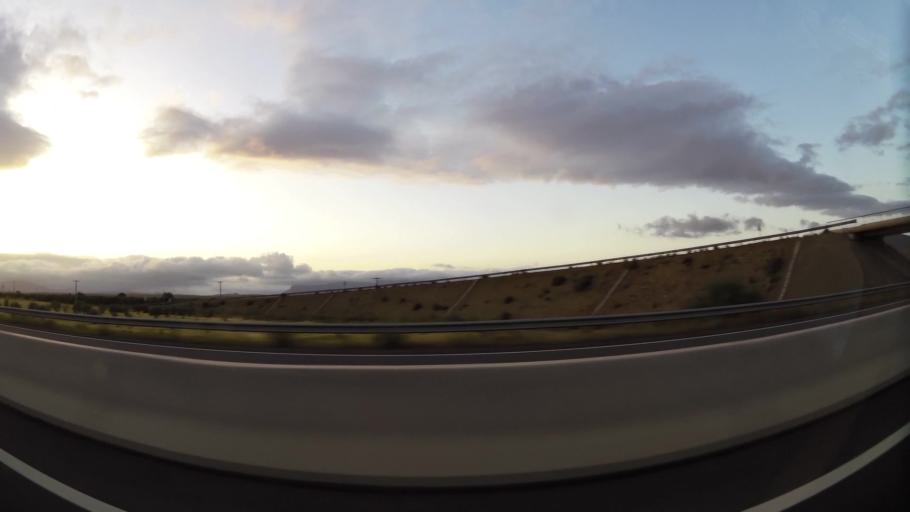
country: MA
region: Oriental
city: El Aioun
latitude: 34.5937
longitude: -2.6953
